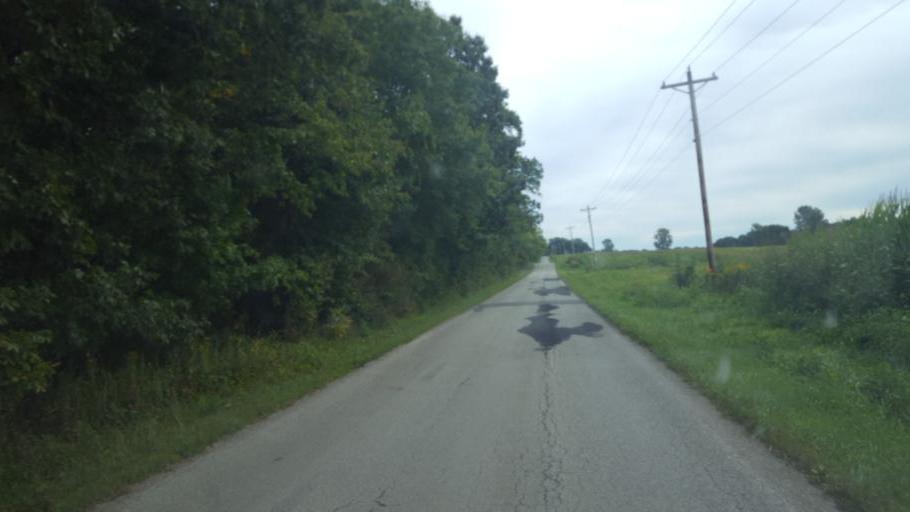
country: US
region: Ohio
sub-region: Knox County
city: Centerburg
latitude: 40.3501
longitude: -82.7563
